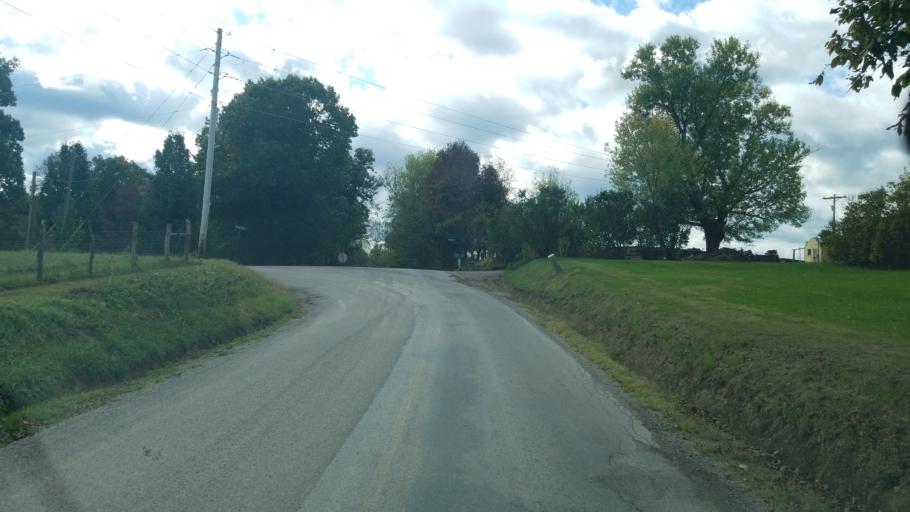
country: US
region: Ohio
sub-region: Vinton County
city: McArthur
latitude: 39.2274
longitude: -82.5084
